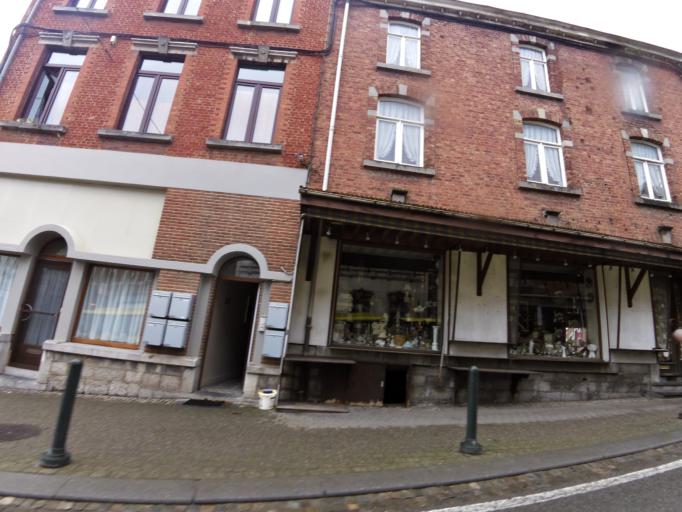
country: BE
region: Wallonia
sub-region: Province de Namur
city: Rochefort
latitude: 50.1565
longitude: 5.2225
